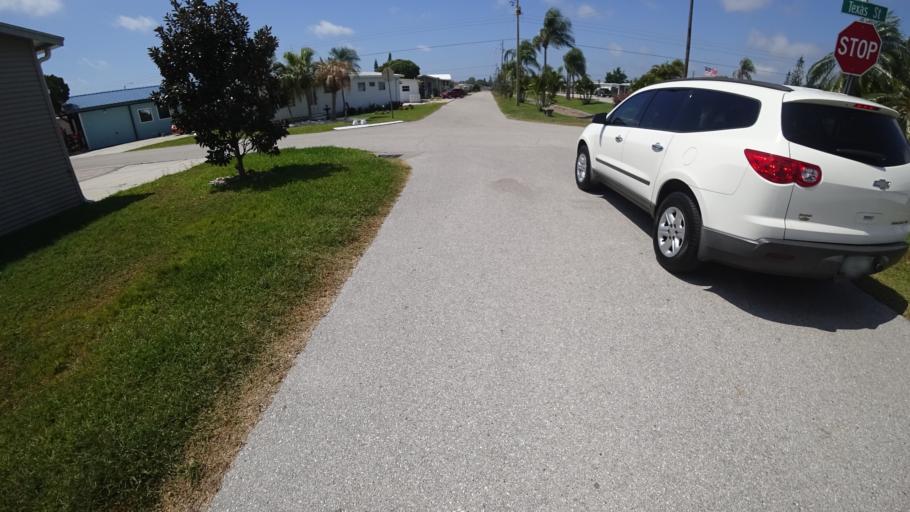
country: US
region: Florida
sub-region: Manatee County
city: Bayshore Gardens
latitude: 27.4242
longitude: -82.5798
